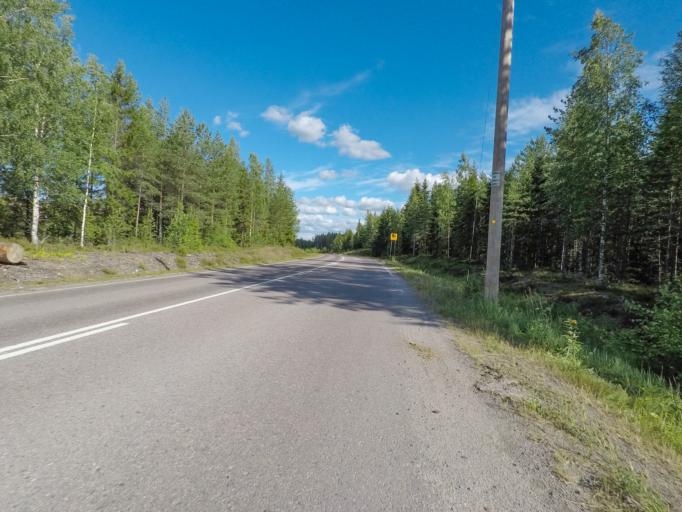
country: FI
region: South Karelia
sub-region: Lappeenranta
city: Joutseno
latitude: 61.1472
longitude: 28.6183
